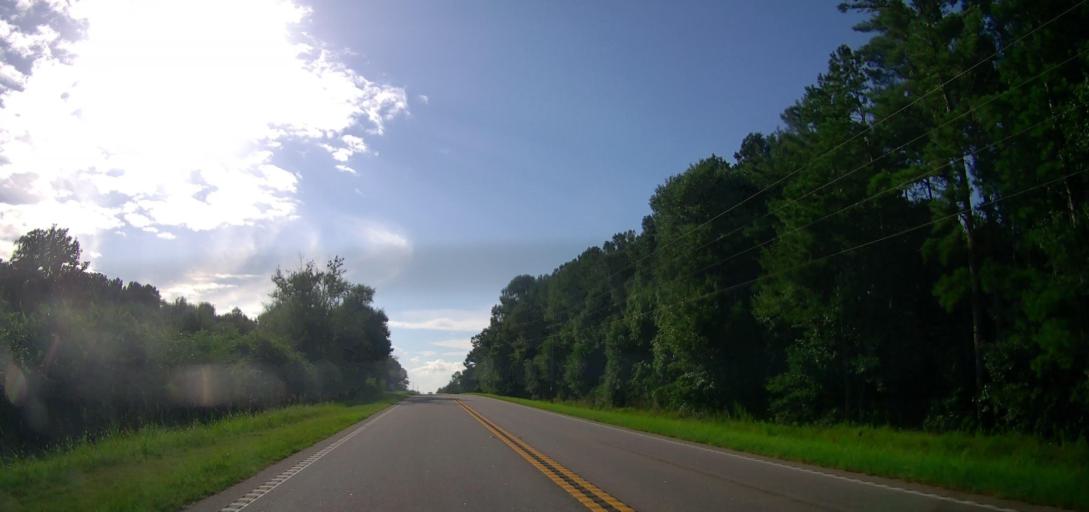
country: US
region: Georgia
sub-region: Coffee County
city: Douglas
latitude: 31.4738
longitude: -82.7786
